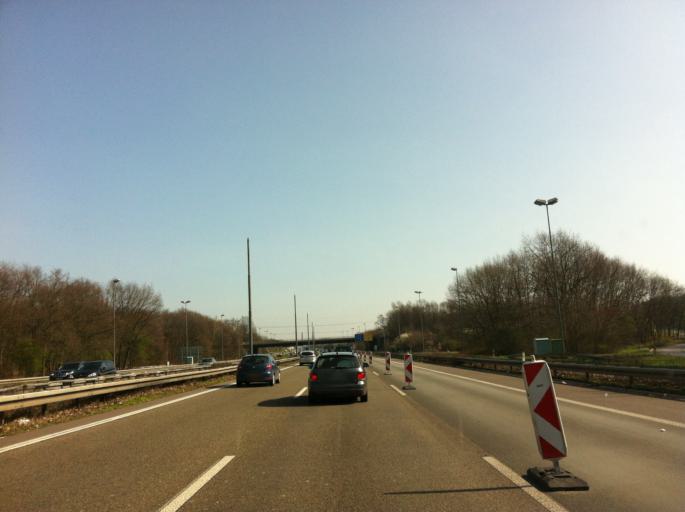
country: DE
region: North Rhine-Westphalia
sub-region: Regierungsbezirk Koln
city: Leverkusen
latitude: 51.0221
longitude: 6.9393
